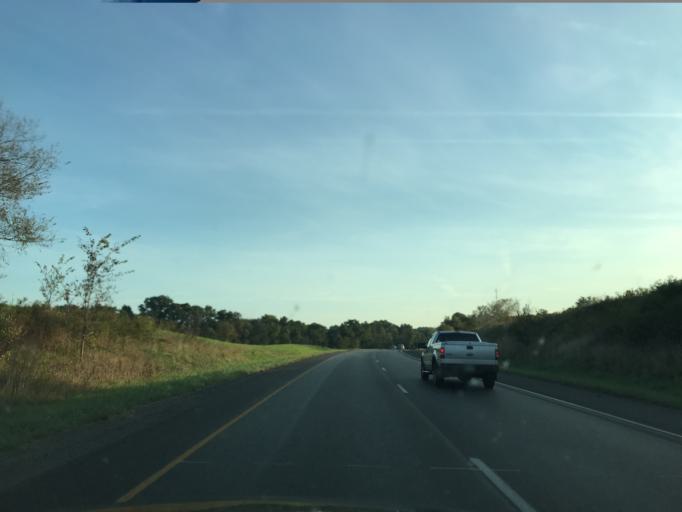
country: US
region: Pennsylvania
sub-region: Butler County
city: Slippery Rock
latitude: 41.0093
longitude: -80.1146
